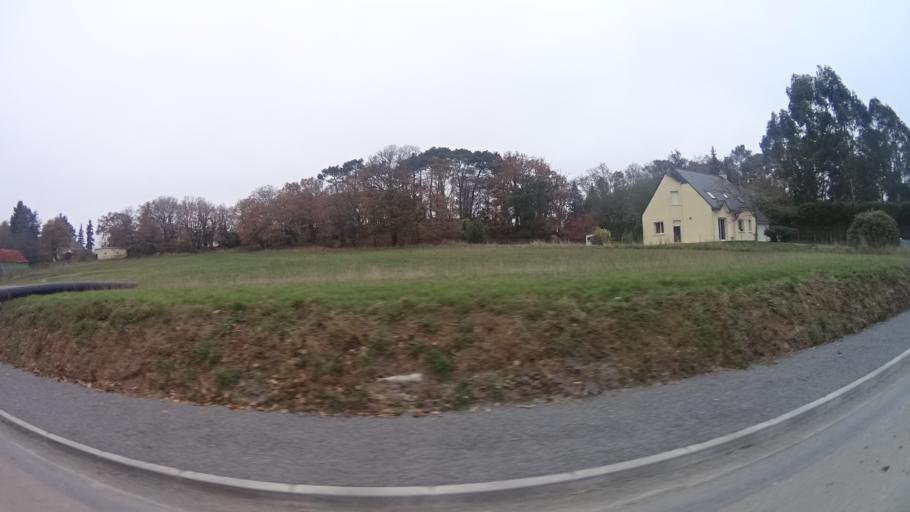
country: FR
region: Brittany
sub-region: Departement d'Ille-et-Vilaine
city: Sainte-Marie
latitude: 47.6811
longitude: -2.0162
